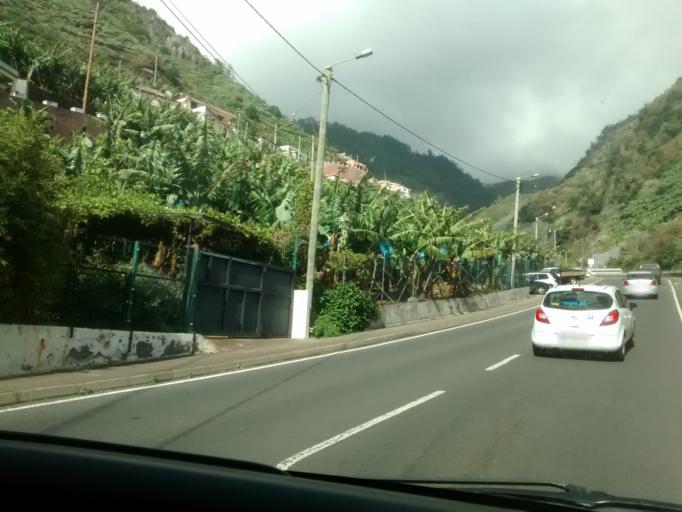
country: PT
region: Madeira
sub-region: Calheta
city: Arco da Calheta
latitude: 32.7032
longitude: -17.1348
